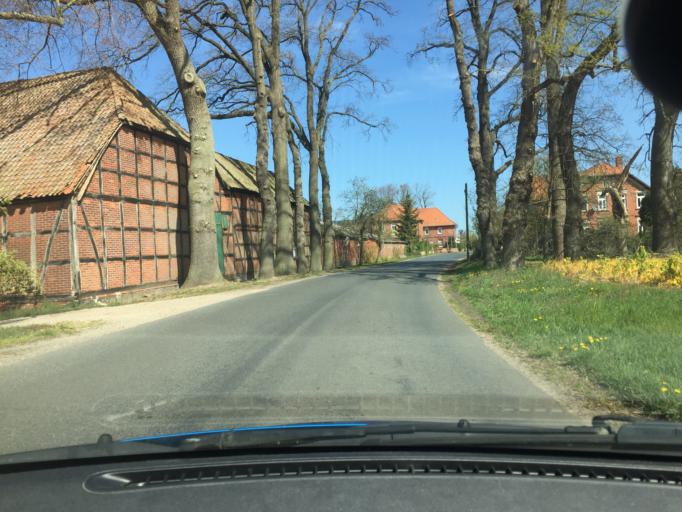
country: DE
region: Lower Saxony
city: Suhlendorf
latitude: 52.9235
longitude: 10.7106
